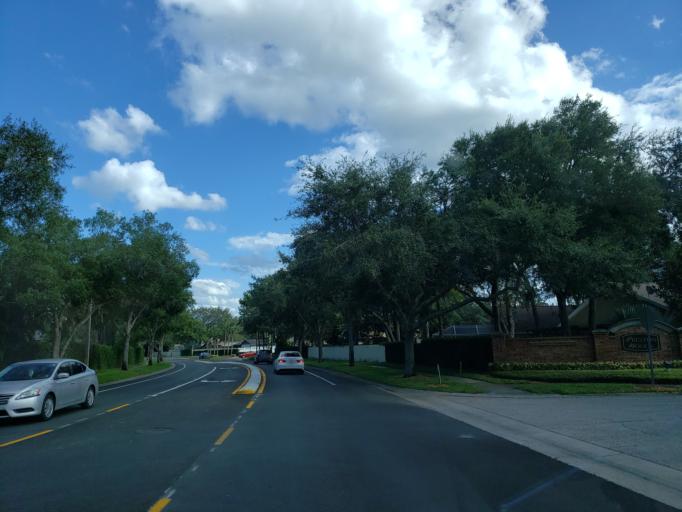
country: US
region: Florida
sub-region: Hillsborough County
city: Bloomingdale
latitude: 27.8763
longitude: -82.2646
